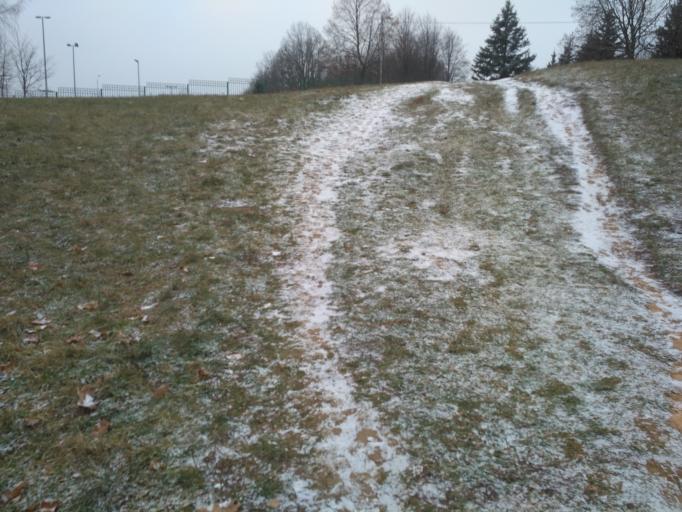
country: BY
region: Minsk
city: Novoye Medvezhino
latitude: 53.9180
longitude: 27.4843
